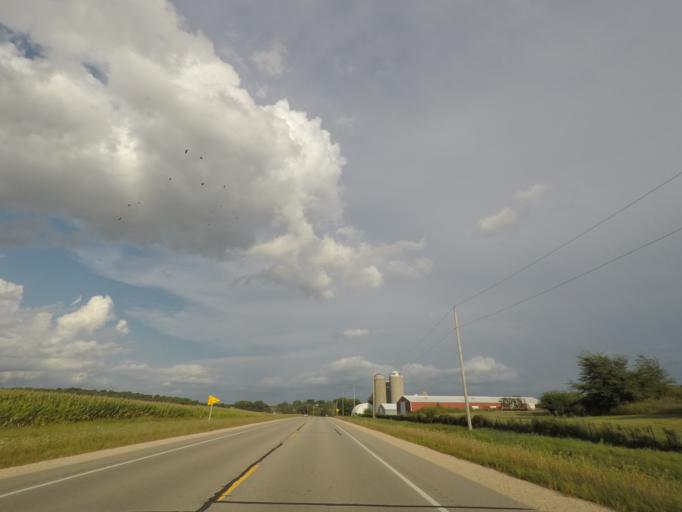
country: US
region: Wisconsin
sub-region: Dane County
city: Waunakee
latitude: 43.1917
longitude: -89.5169
